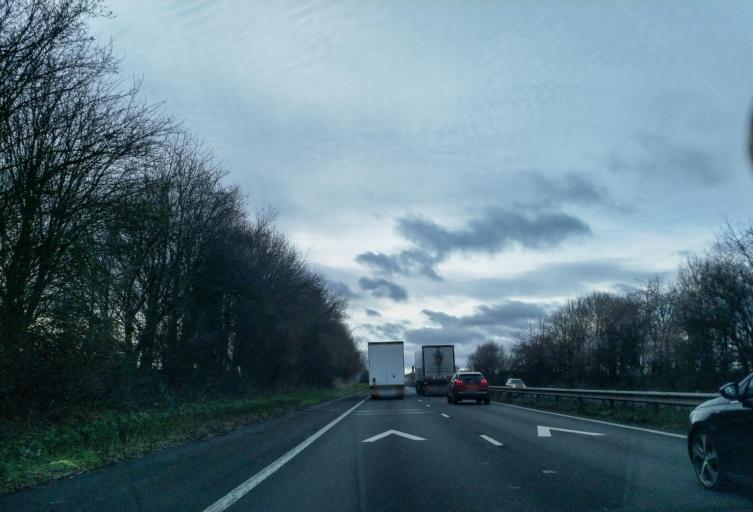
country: GB
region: England
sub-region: Kent
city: Sittingbourne
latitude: 51.2972
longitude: 0.7632
